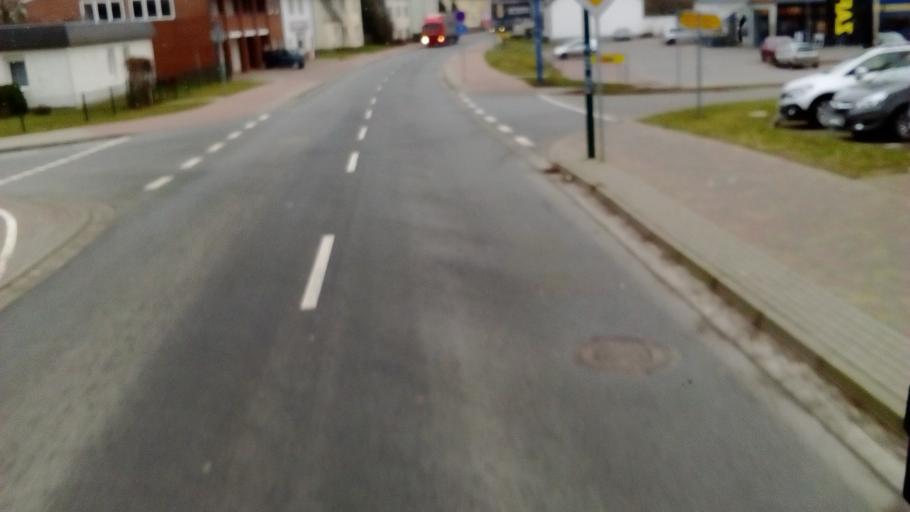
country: DE
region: Mecklenburg-Vorpommern
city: Strasburg
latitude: 53.5059
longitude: 13.7498
